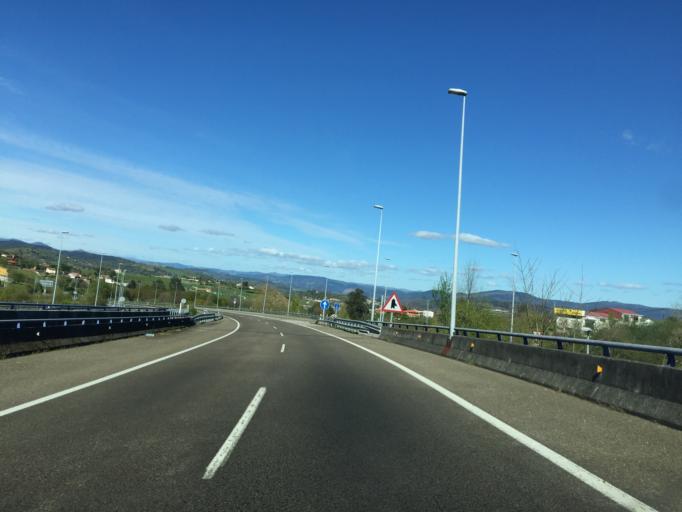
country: ES
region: Asturias
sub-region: Province of Asturias
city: Oviedo
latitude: 43.3474
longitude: -5.8957
